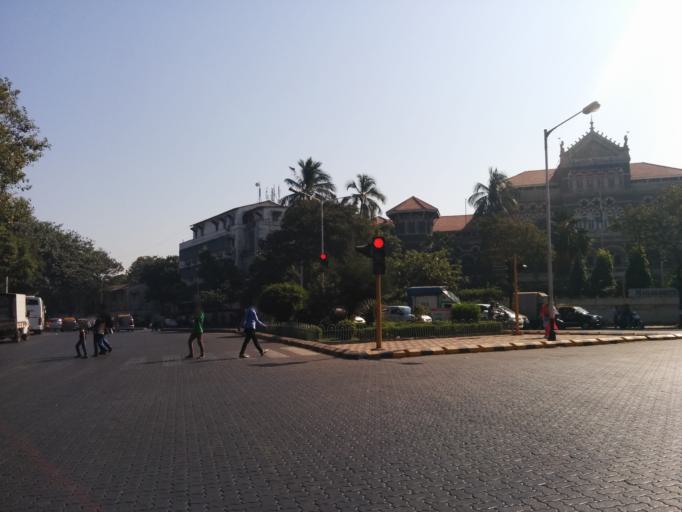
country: IN
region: Maharashtra
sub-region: Raigarh
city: Uran
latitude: 18.9256
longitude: 72.8324
